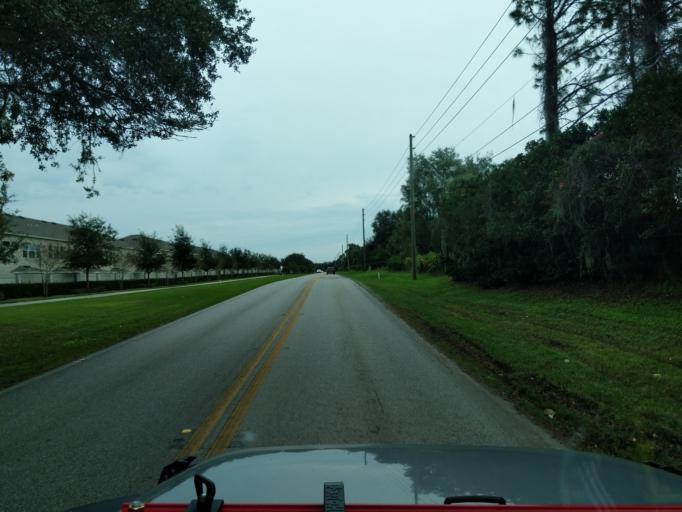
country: US
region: Florida
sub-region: Orange County
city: Oakland
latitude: 28.5254
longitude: -81.6177
